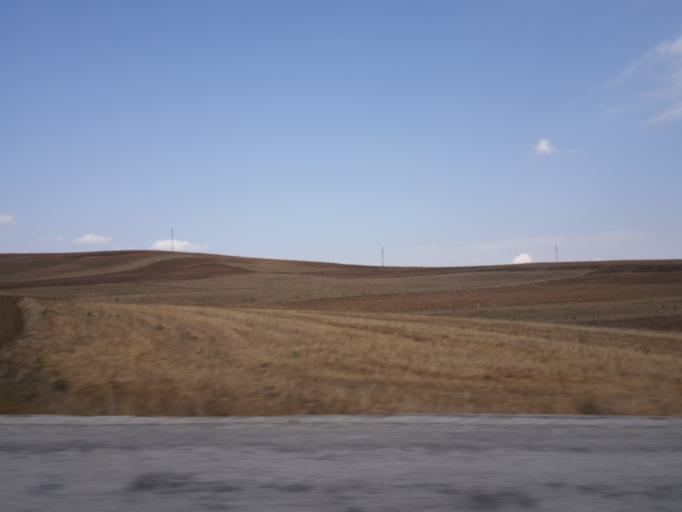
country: TR
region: Corum
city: Alaca
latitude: 40.1577
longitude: 34.7180
